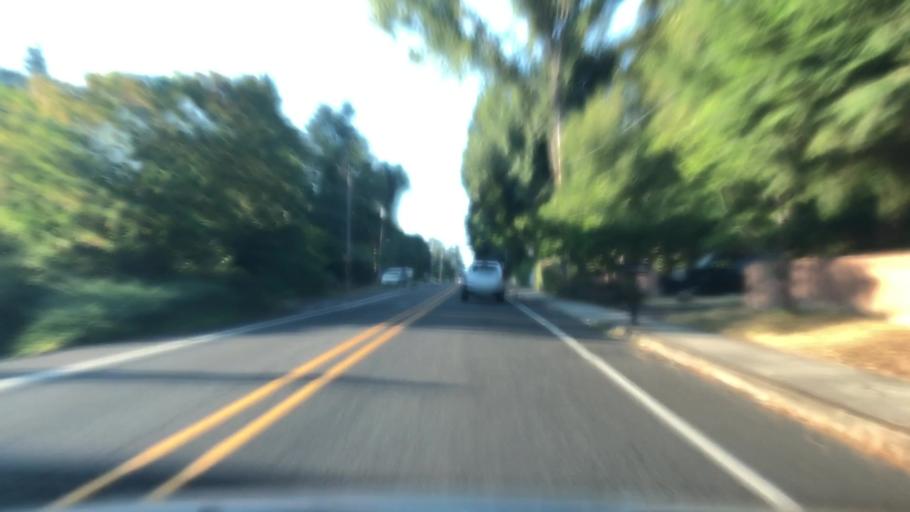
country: US
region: Oregon
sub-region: Clackamas County
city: Oak Grove
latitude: 45.4131
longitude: -122.6455
